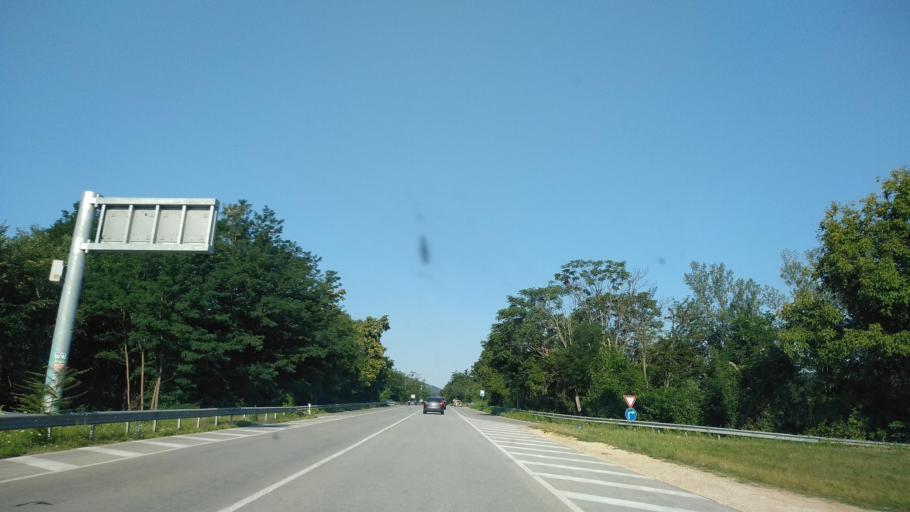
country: BG
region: Lovech
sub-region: Obshtina Lovech
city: Lovech
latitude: 43.0409
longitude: 24.7194
